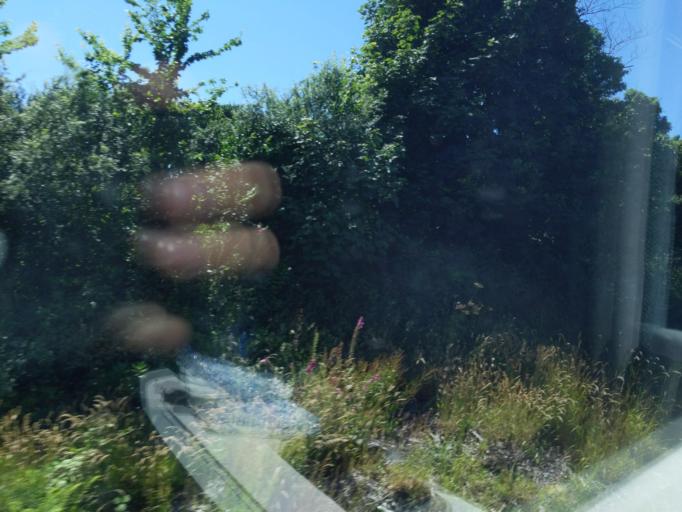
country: GB
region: England
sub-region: Cornwall
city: Chacewater
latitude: 50.2640
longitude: -5.1712
